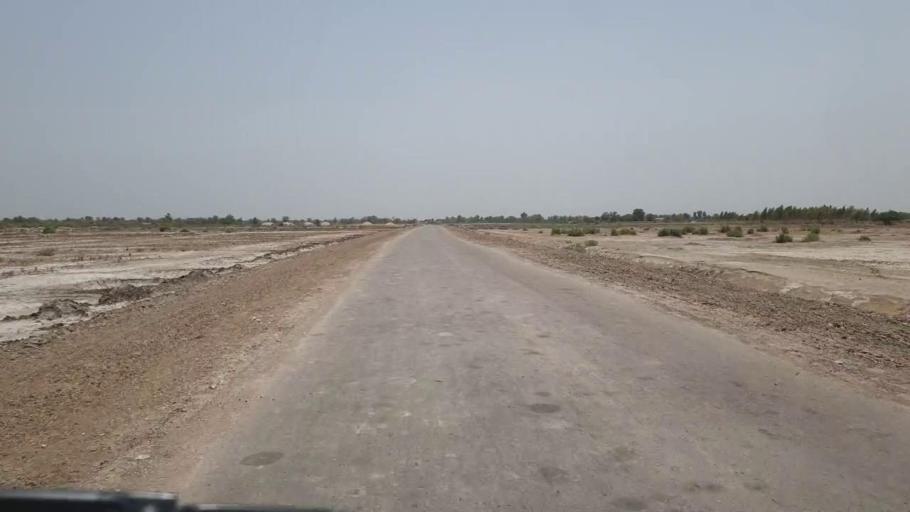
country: PK
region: Sindh
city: Daulatpur
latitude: 26.4552
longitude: 68.1181
